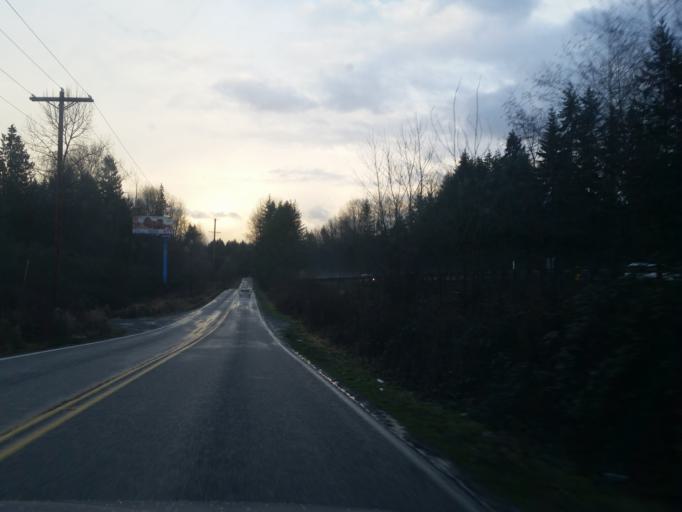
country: US
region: Washington
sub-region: Snohomish County
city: Maltby
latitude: 47.8108
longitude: -122.1058
